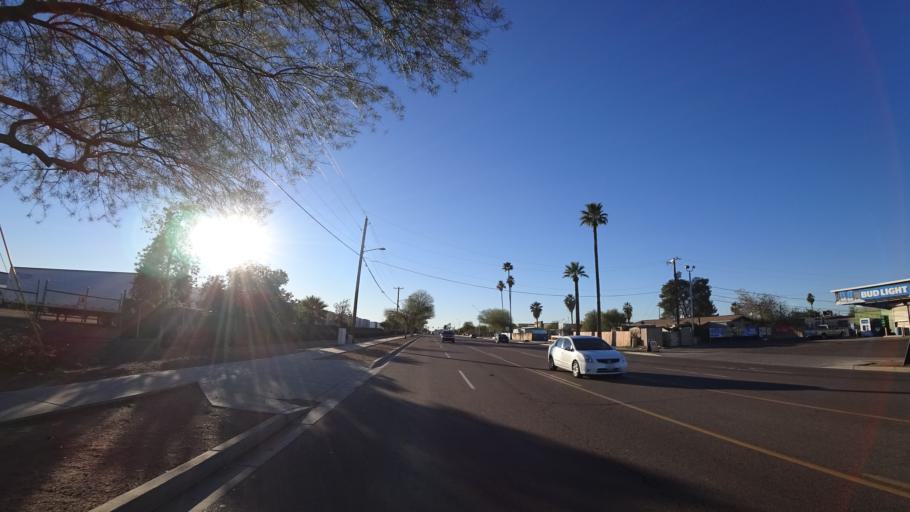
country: US
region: Arizona
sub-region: Maricopa County
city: Tolleson
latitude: 33.4515
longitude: -112.1994
